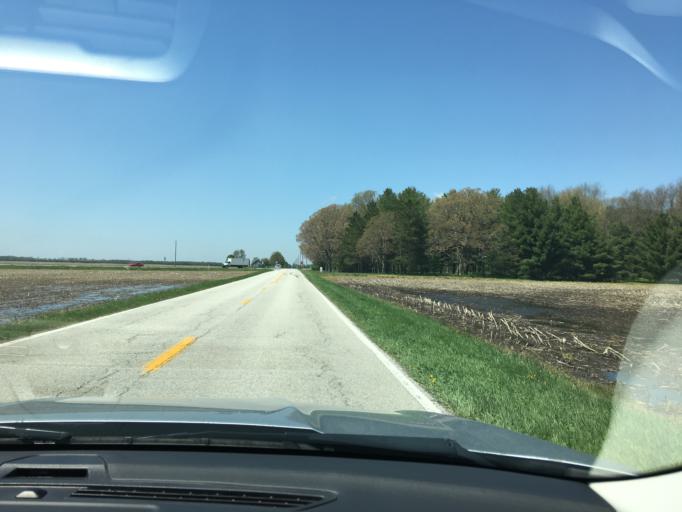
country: US
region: Indiana
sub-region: Tippecanoe County
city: Dayton
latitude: 40.3159
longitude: -86.7640
